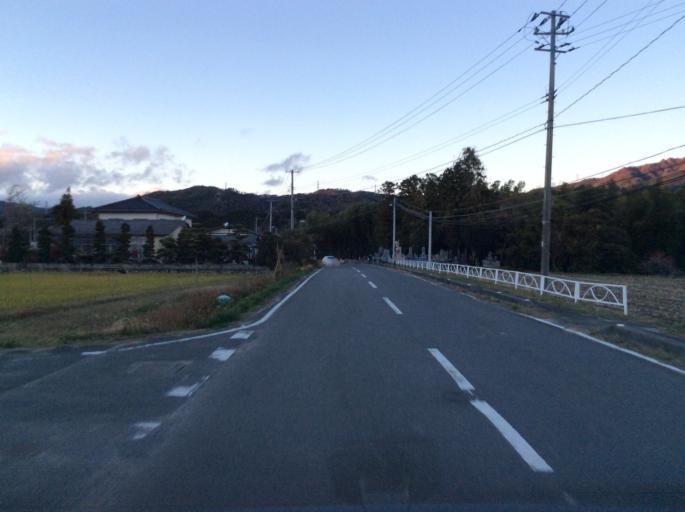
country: JP
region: Fukushima
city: Iwaki
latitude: 37.1325
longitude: 140.8508
